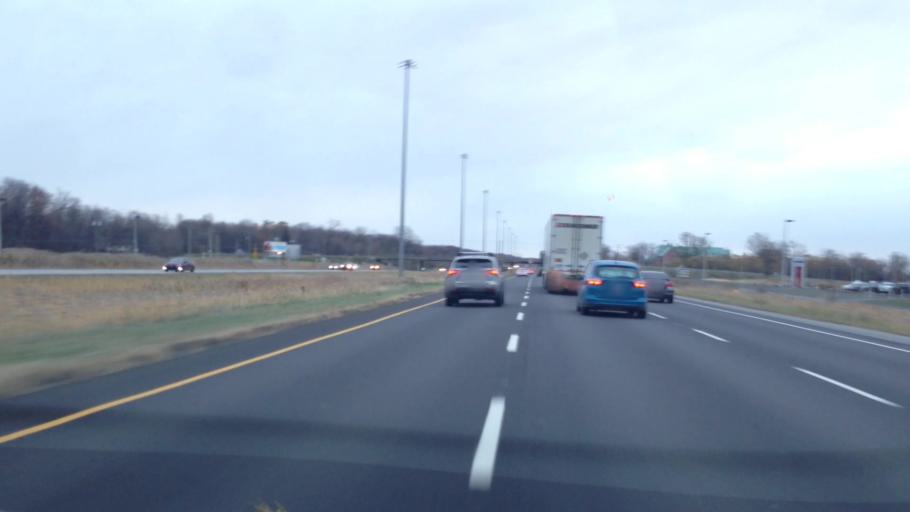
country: CA
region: Quebec
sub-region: Monteregie
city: Vaudreuil-Dorion
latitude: 45.4158
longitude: -74.0208
